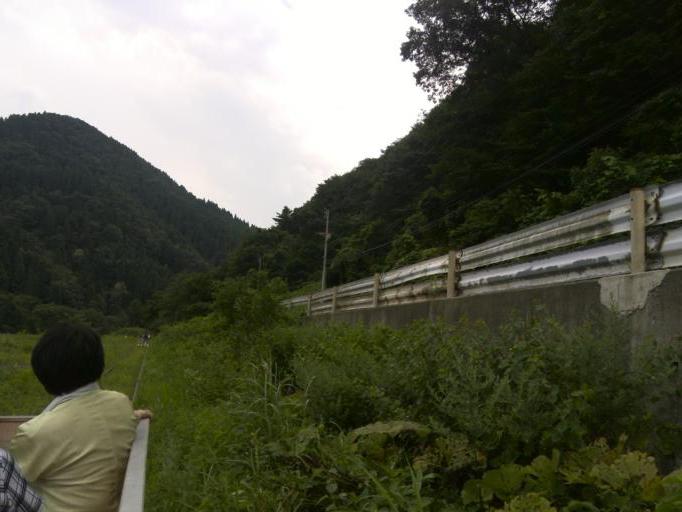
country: JP
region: Akita
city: Odate
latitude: 40.2943
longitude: 140.6367
